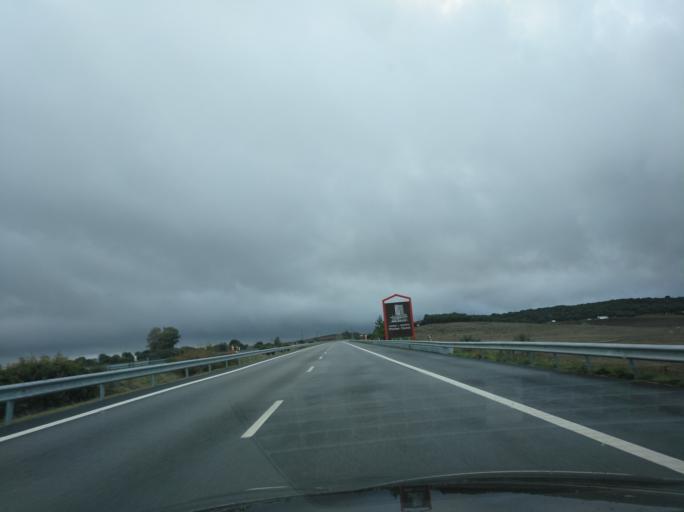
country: PT
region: Evora
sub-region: Borba
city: Borba
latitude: 38.8250
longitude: -7.4396
